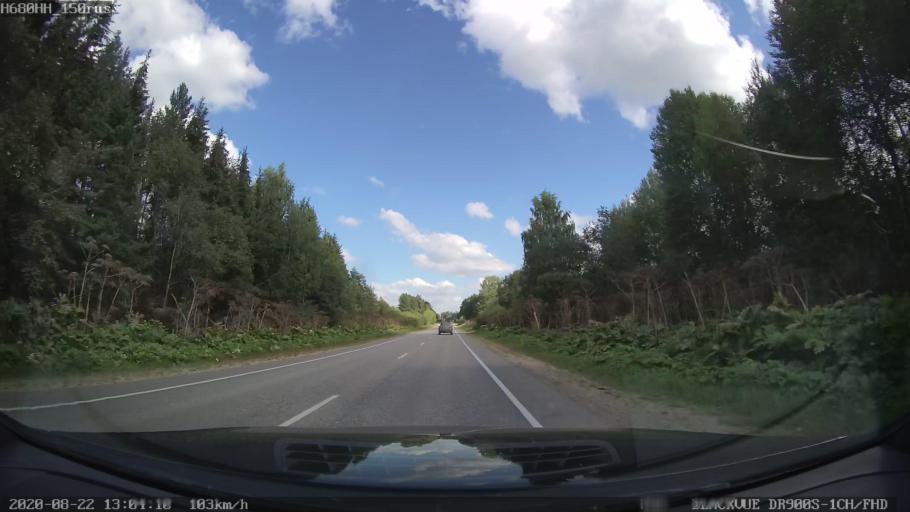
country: RU
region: Tverskaya
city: Bezhetsk
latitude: 57.6643
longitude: 36.4245
